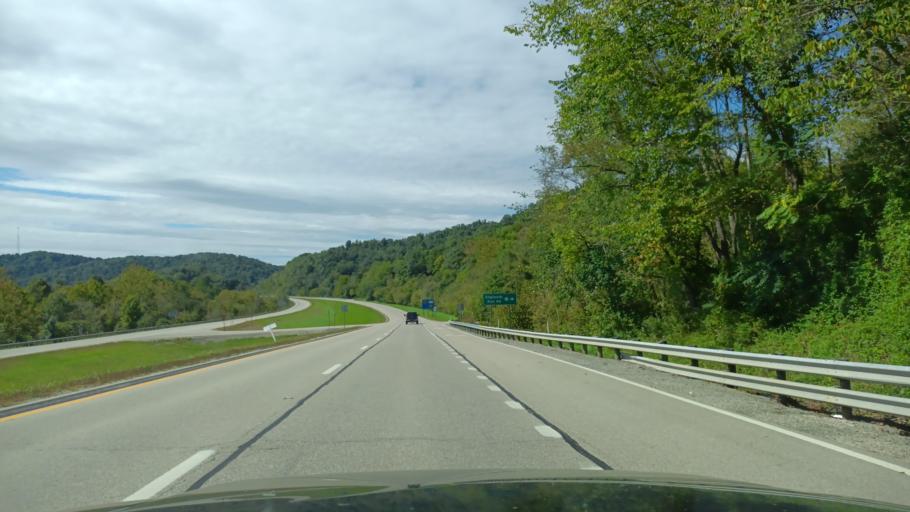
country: US
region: West Virginia
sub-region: Doddridge County
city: West Union
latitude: 39.2871
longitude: -80.7130
